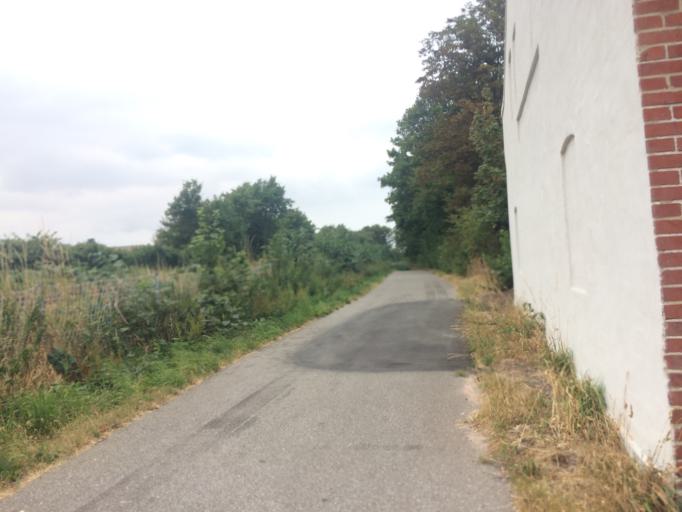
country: DK
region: Central Jutland
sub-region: Struer Kommune
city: Struer
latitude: 56.4805
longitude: 8.6101
